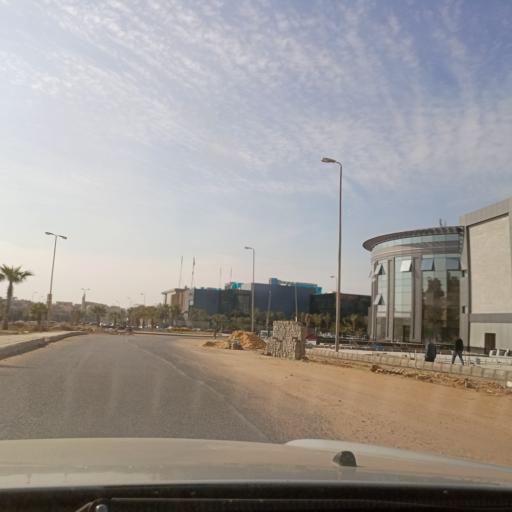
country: EG
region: Muhafazat al Qalyubiyah
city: Al Khankah
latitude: 30.0459
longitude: 31.4863
